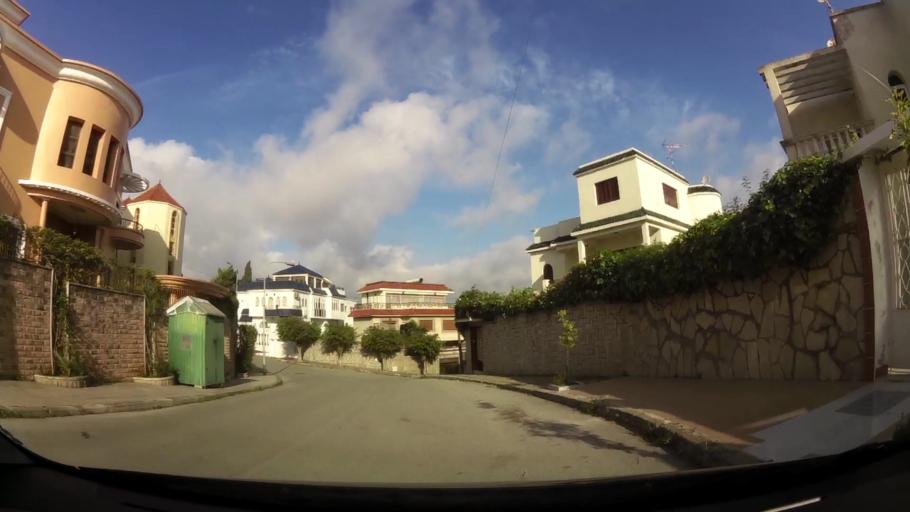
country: MA
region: Tanger-Tetouan
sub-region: Tanger-Assilah
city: Tangier
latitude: 35.7692
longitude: -5.7966
